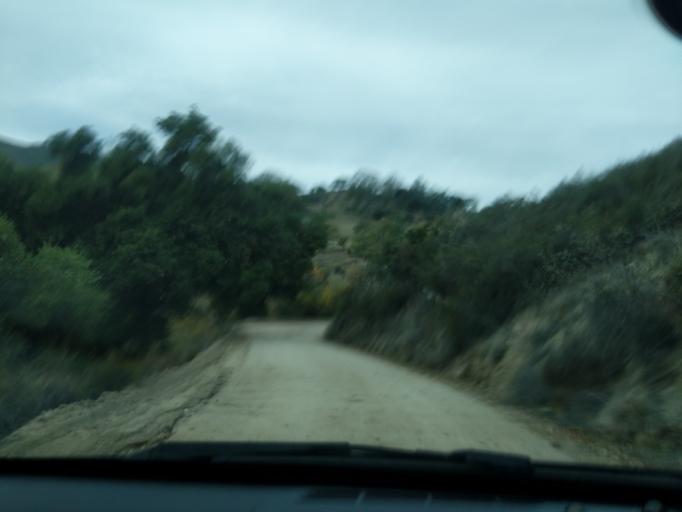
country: US
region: California
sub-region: Monterey County
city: Soledad
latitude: 36.5642
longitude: -121.2034
